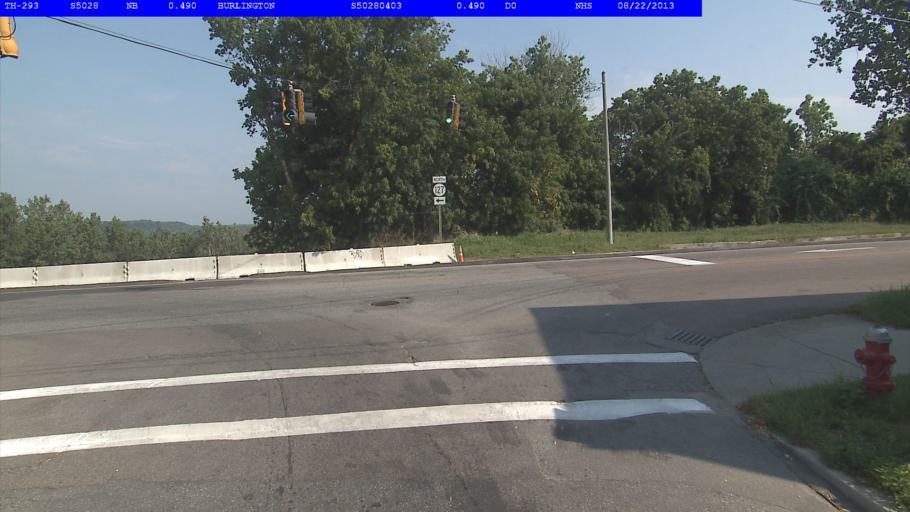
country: US
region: Vermont
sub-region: Chittenden County
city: Burlington
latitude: 44.4874
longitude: -73.2179
